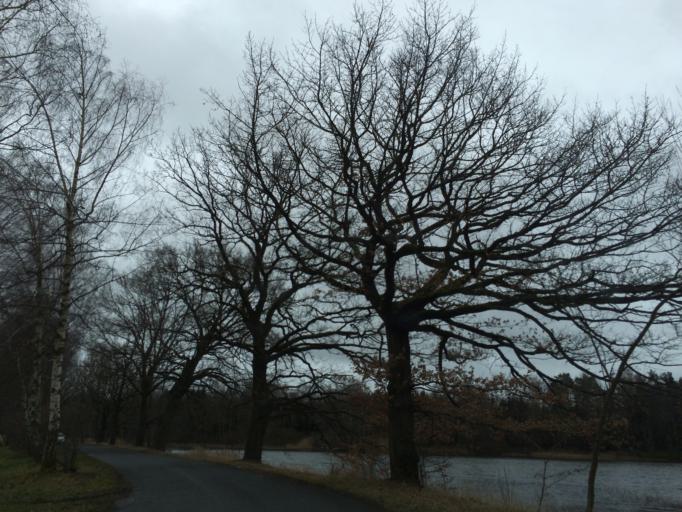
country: DE
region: Thuringia
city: Plothen
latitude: 50.6483
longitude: 11.7605
